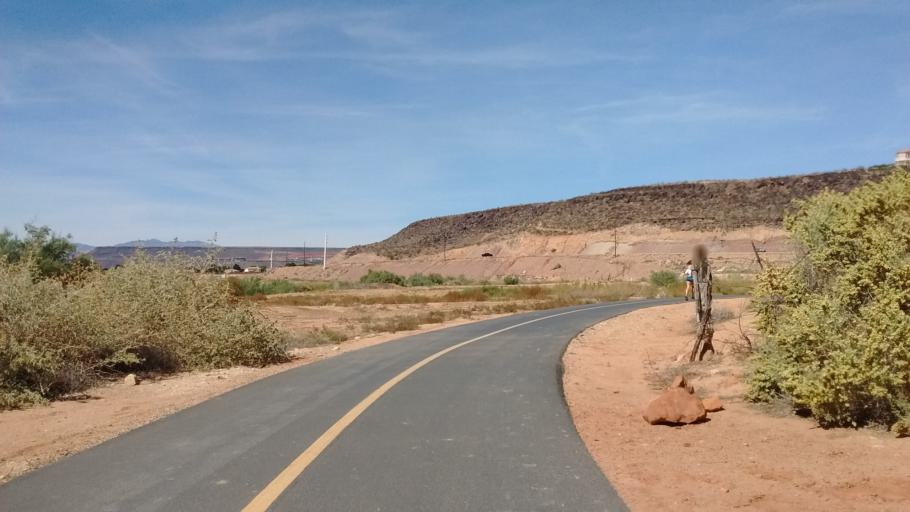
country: US
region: Utah
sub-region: Washington County
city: Saint George
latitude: 37.0861
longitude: -113.5443
